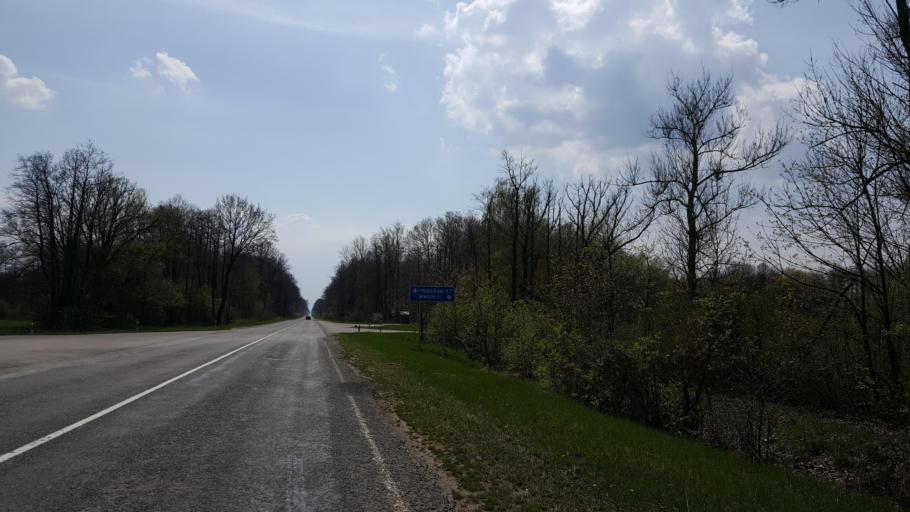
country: BY
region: Brest
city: Zhabinka
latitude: 52.2868
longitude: 23.9440
